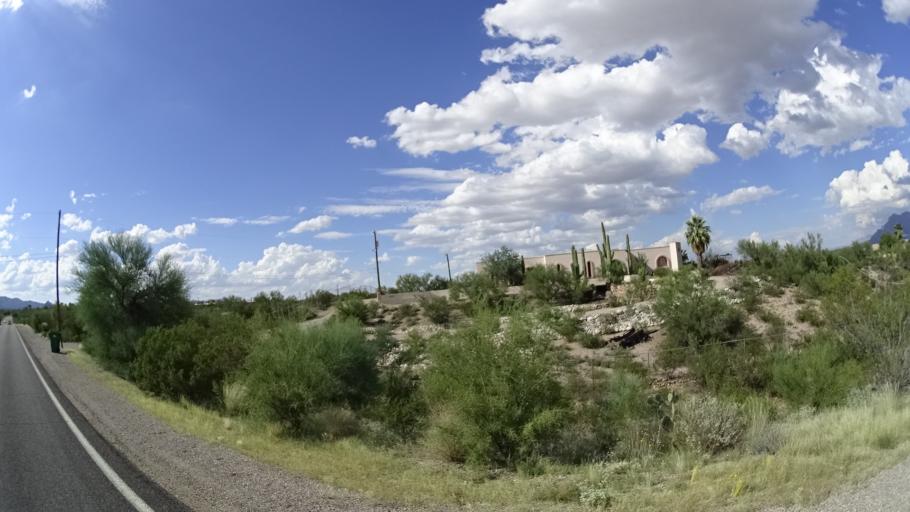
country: US
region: Arizona
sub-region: Pima County
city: Flowing Wells
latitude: 32.2798
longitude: -111.0410
